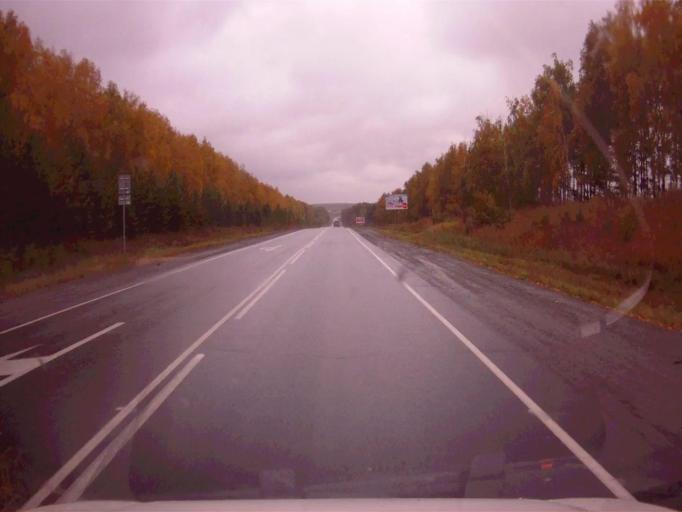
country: RU
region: Chelyabinsk
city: Roshchino
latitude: 55.3617
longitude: 61.2161
